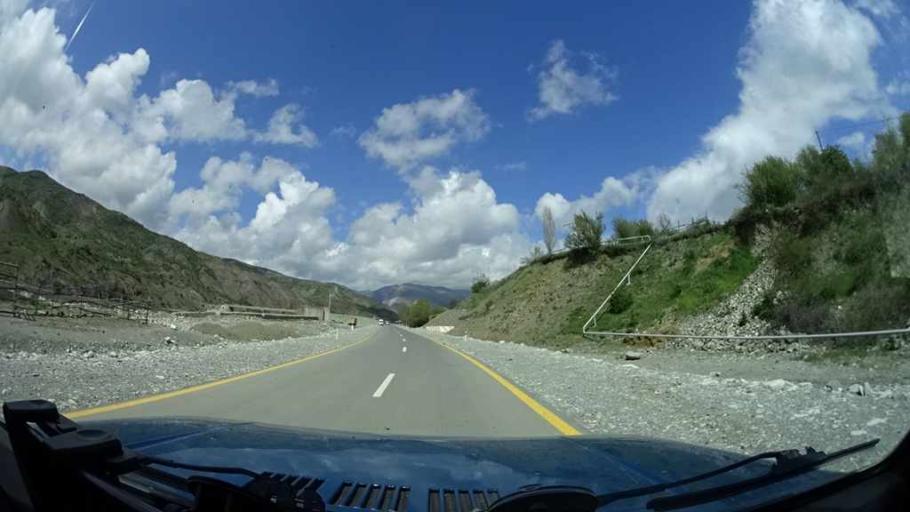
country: AZ
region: Ismayilli
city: Basqal
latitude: 40.8487
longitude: 48.3831
